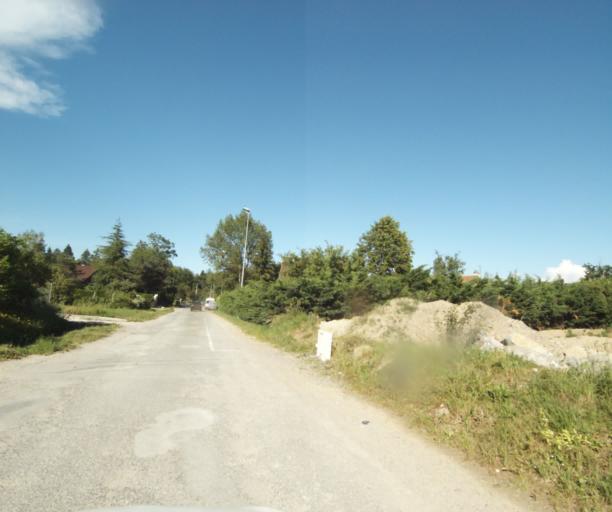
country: FR
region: Rhone-Alpes
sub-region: Departement de la Haute-Savoie
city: Sciez
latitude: 46.3409
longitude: 6.3550
